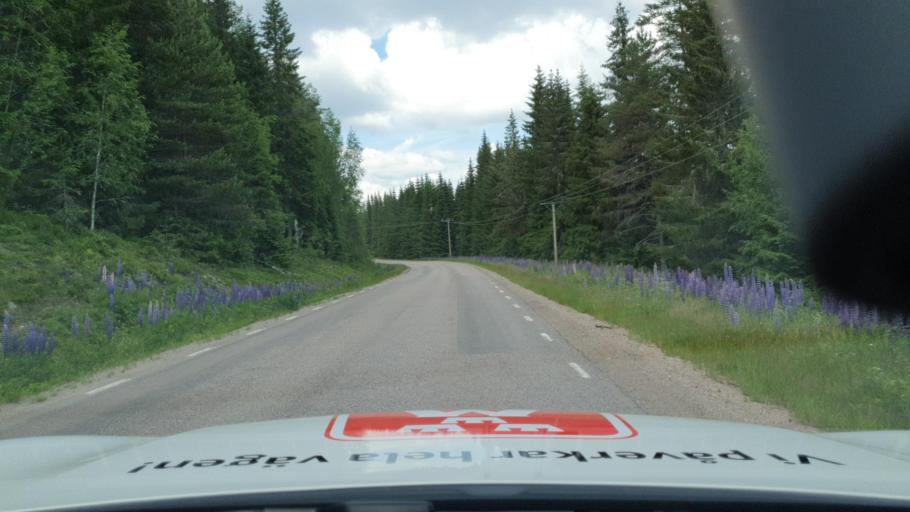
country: SE
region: Vaermland
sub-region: Torsby Kommun
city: Torsby
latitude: 60.4886
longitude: 12.8734
